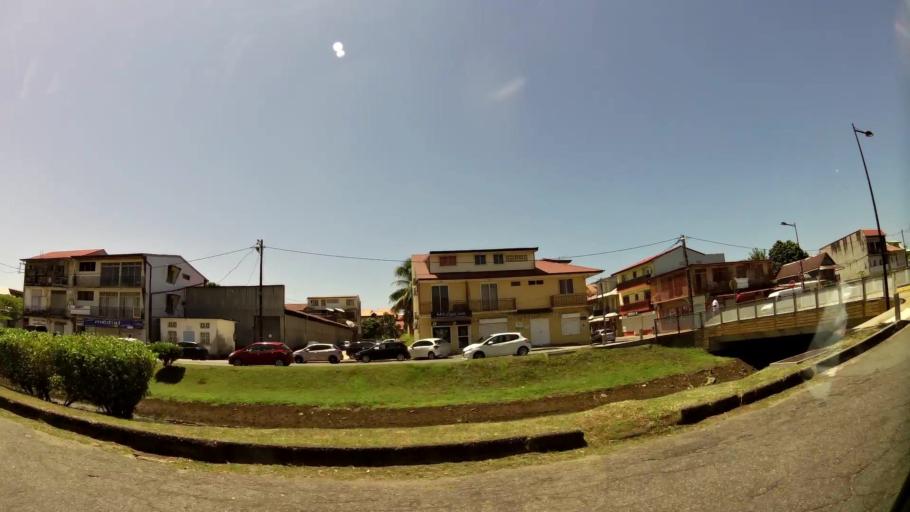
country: GF
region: Guyane
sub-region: Guyane
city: Cayenne
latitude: 4.9359
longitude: -52.3299
